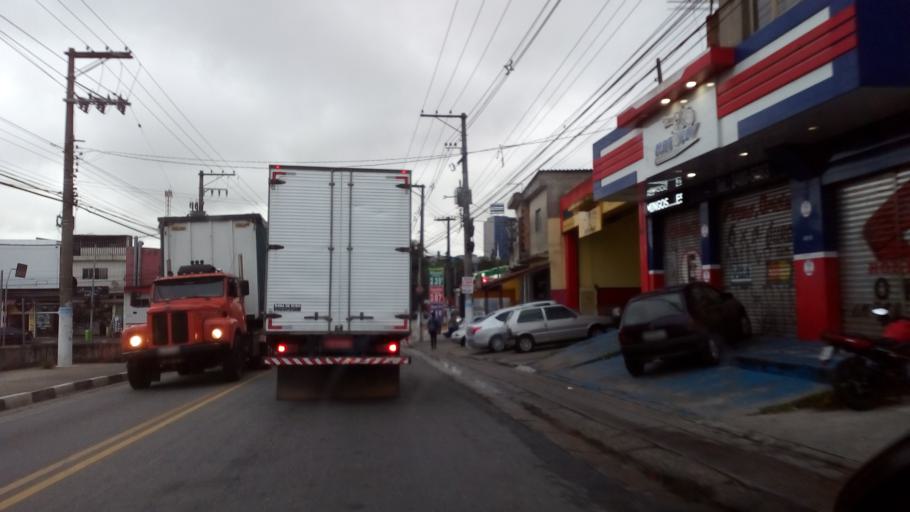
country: BR
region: Sao Paulo
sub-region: Itaquaquecetuba
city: Itaquaquecetuba
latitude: -23.4357
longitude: -46.4069
